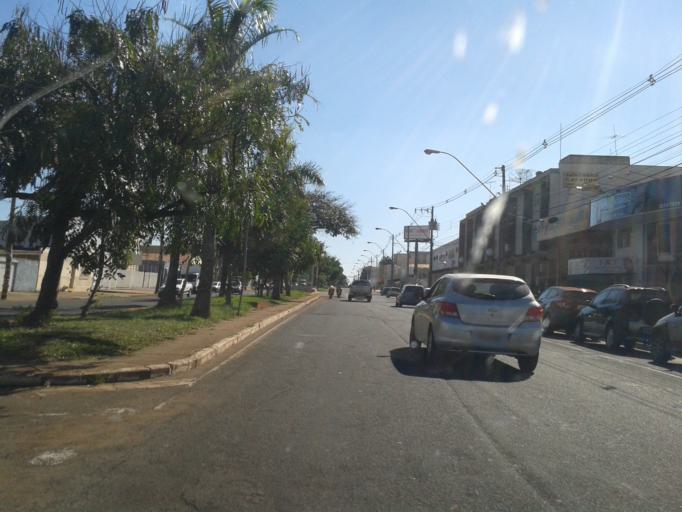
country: BR
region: Minas Gerais
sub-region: Uberaba
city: Uberaba
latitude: -19.7440
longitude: -47.9554
